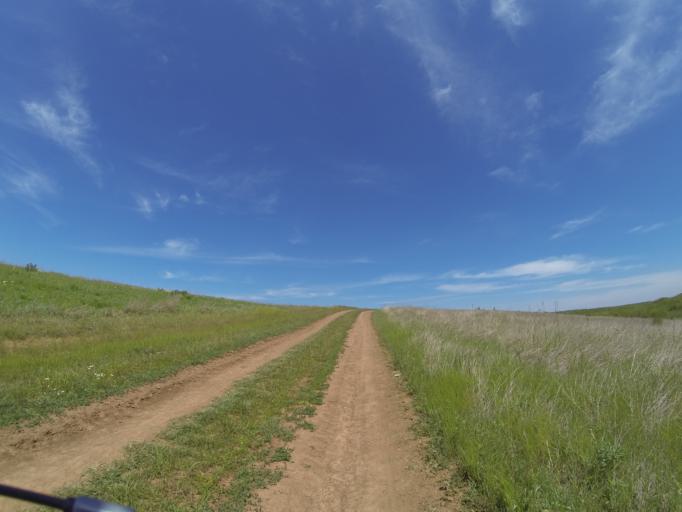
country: RO
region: Dolj
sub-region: Comuna Teslui
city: Teslui
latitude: 44.1786
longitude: 24.1699
